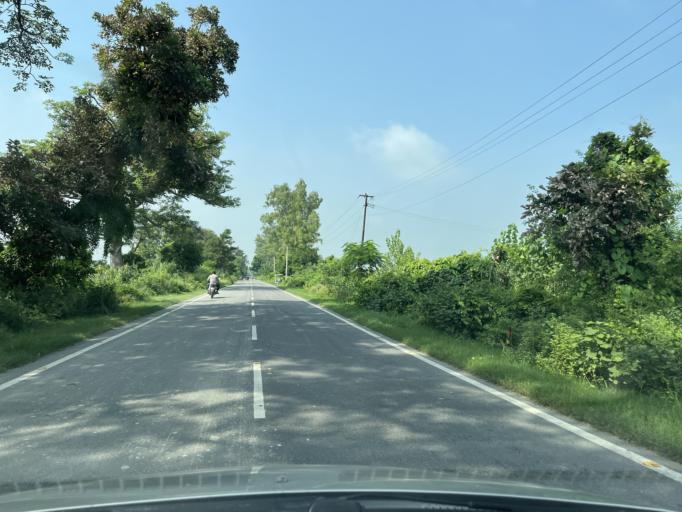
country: IN
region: Uttarakhand
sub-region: Udham Singh Nagar
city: Bazpur
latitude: 29.1866
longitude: 79.1859
